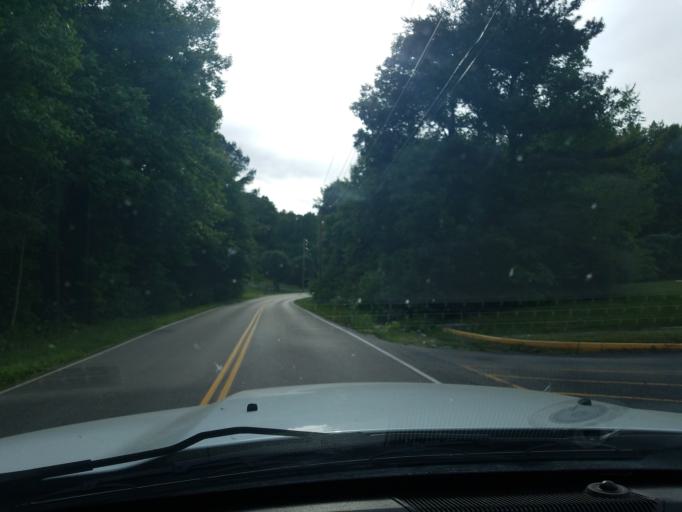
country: US
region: Tennessee
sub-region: Putnam County
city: Cookeville
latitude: 36.1330
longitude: -85.5362
